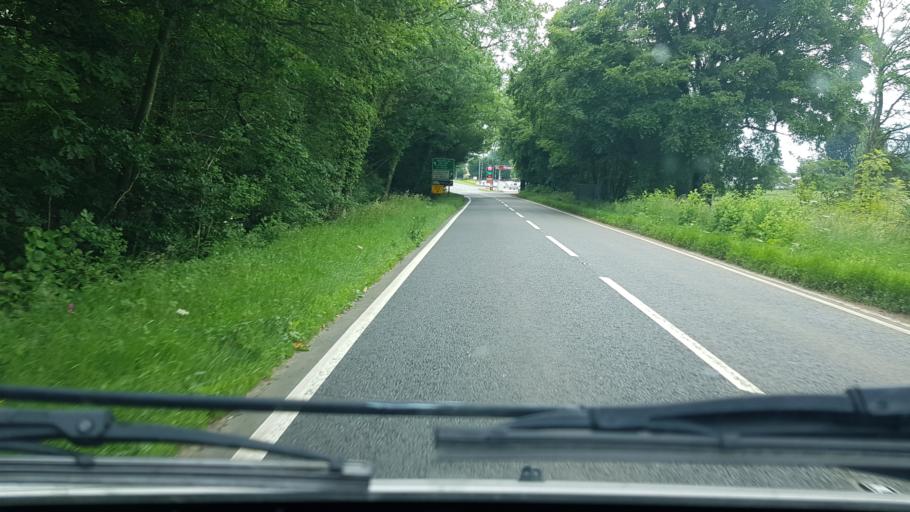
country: GB
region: England
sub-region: Gloucestershire
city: Chipping Campden
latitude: 51.9992
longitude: -1.7843
